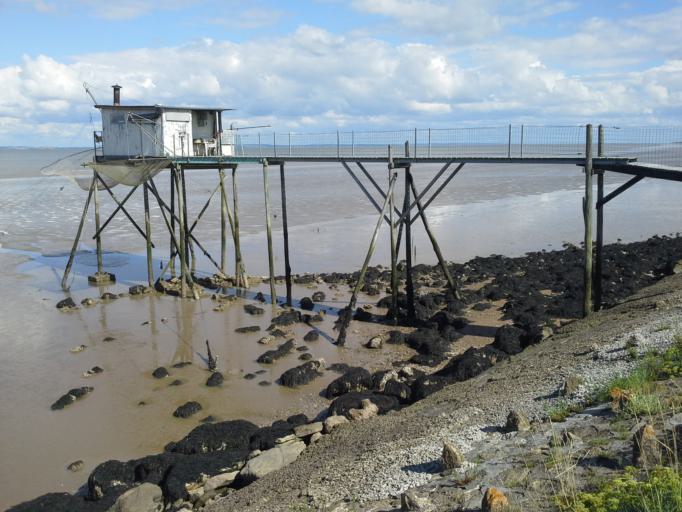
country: FR
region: Aquitaine
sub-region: Departement de la Gironde
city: Gaillan-en-Medoc
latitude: 45.4305
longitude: -0.9240
